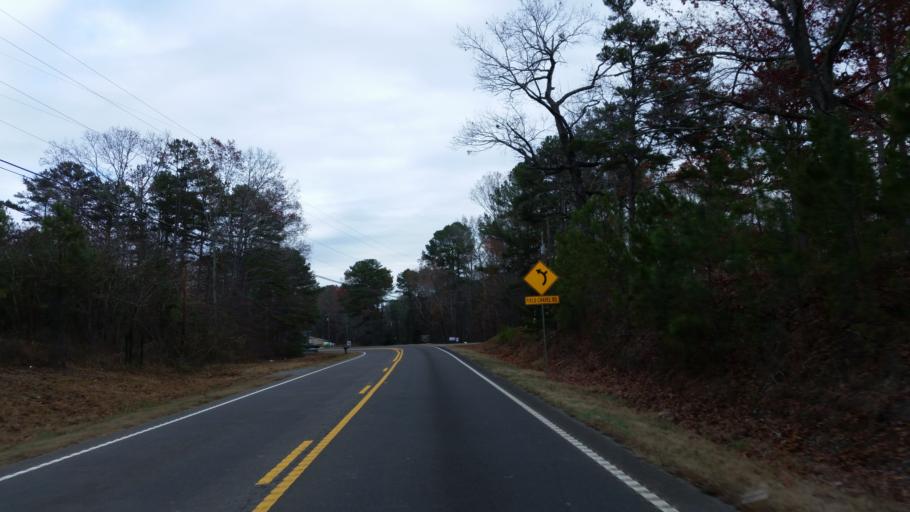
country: US
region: Georgia
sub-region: Cherokee County
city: Holly Springs
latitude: 34.2112
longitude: -84.5945
